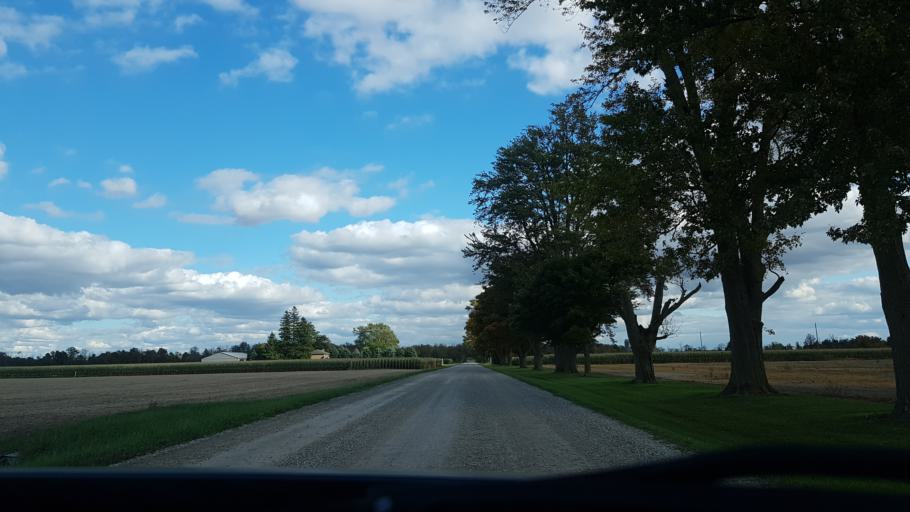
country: CA
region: Ontario
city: South Huron
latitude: 43.1079
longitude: -81.6192
